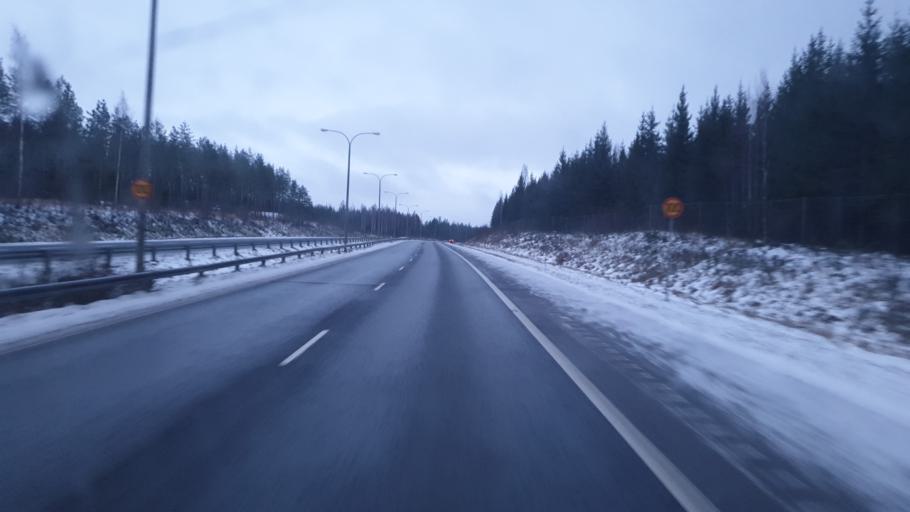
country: FI
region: Northern Savo
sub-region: Kuopio
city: Siilinjaervi
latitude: 63.0152
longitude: 27.6685
